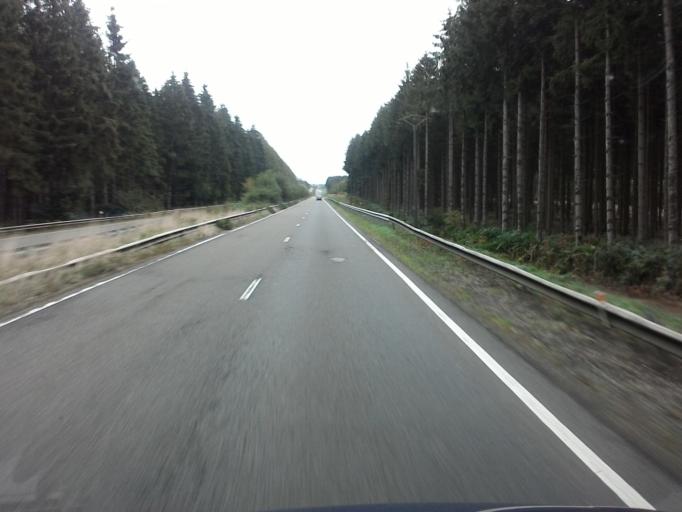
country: BE
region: Wallonia
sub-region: Province du Luxembourg
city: Bertrix
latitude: 49.8946
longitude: 5.3059
